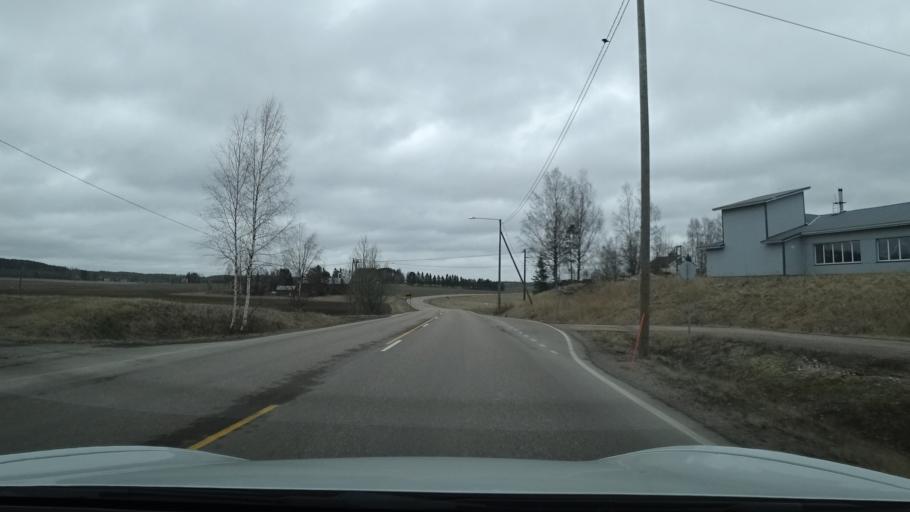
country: FI
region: Uusimaa
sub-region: Porvoo
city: Myrskylae
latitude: 60.6736
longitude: 25.8758
